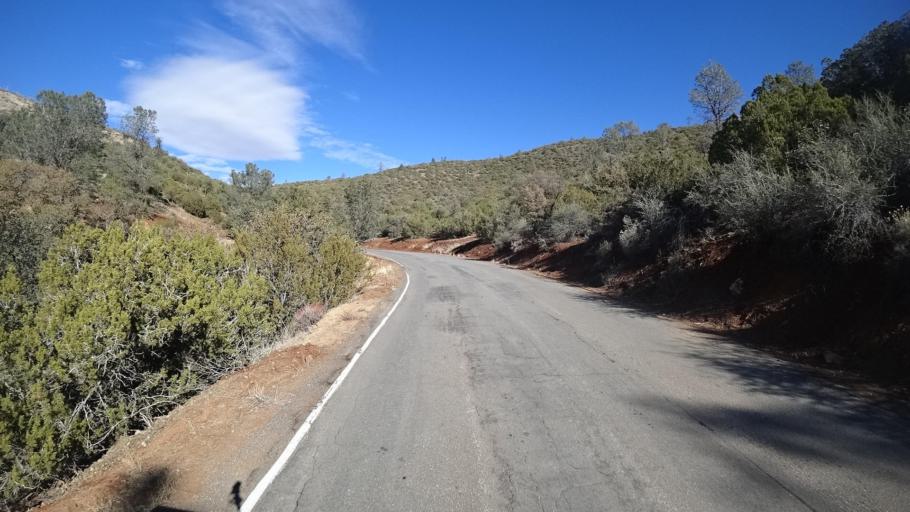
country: US
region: California
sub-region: Kern County
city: Bodfish
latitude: 35.5656
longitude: -118.5030
